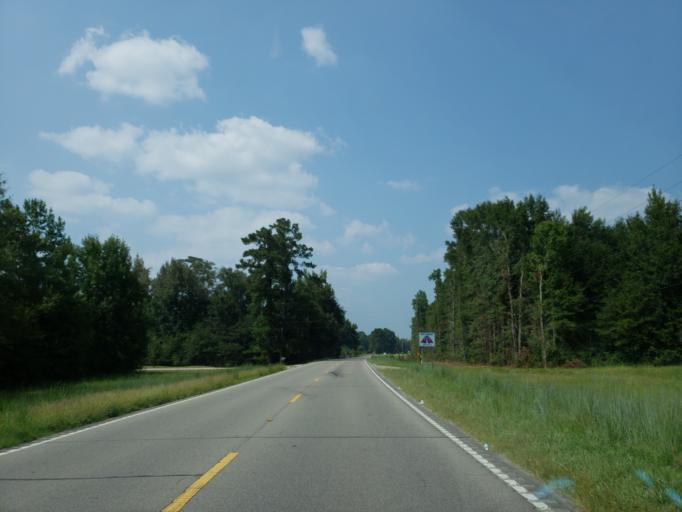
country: US
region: Mississippi
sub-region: Forrest County
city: Glendale
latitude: 31.4440
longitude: -89.2865
